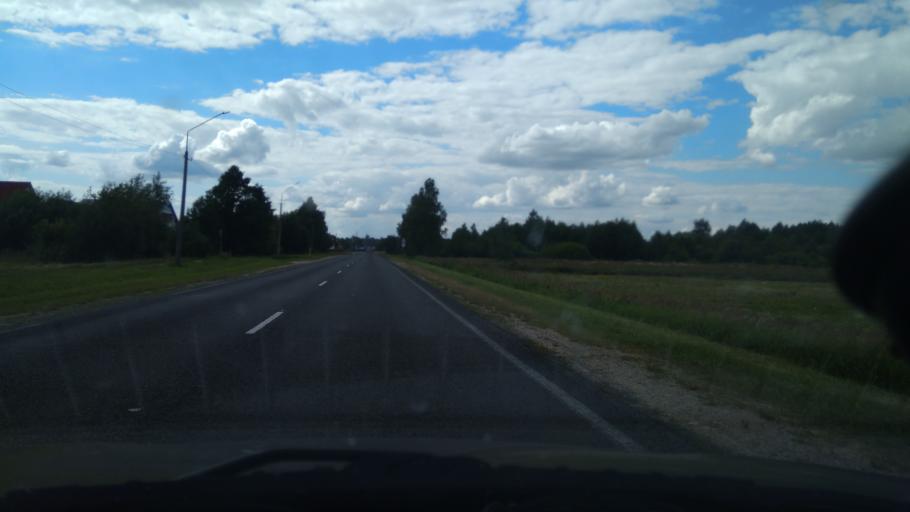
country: BY
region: Grodnenskaya
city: Masty
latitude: 53.4251
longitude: 24.5510
